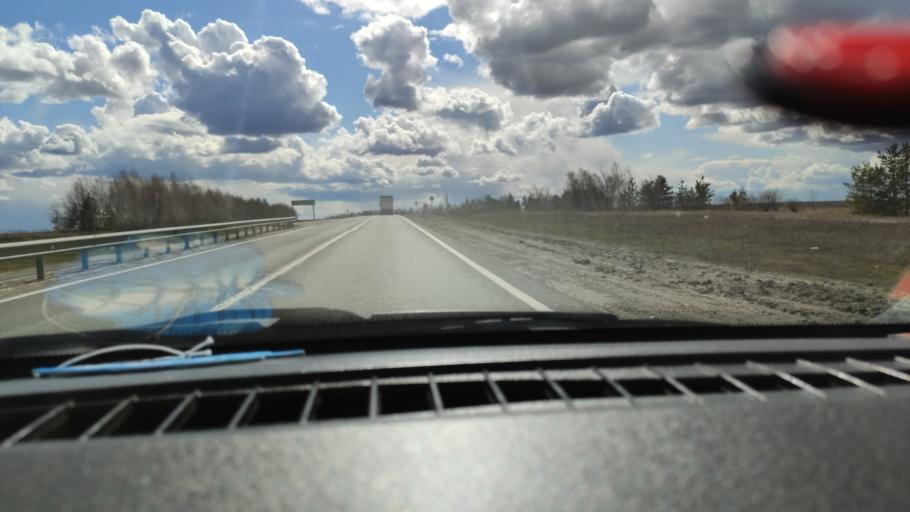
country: RU
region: Saratov
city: Dukhovnitskoye
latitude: 52.8358
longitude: 48.2417
